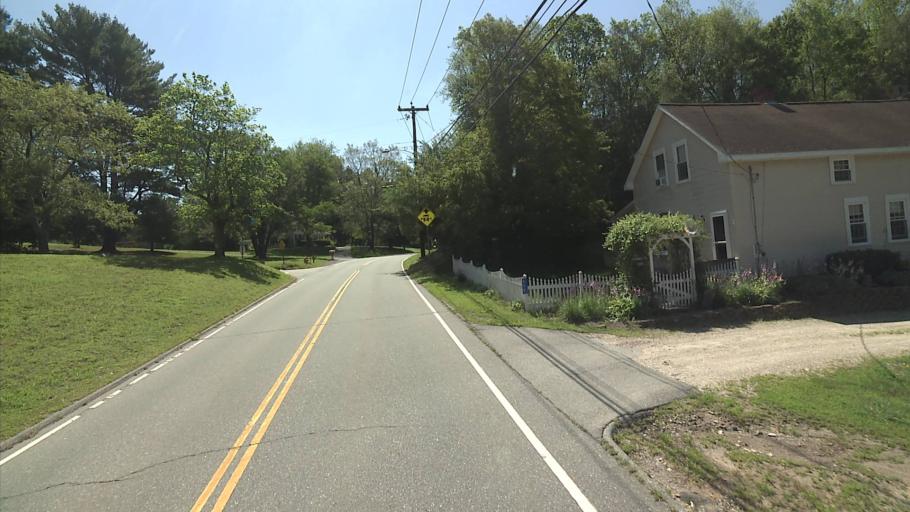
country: US
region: Connecticut
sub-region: Windham County
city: Moosup
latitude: 41.7050
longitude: -71.8225
